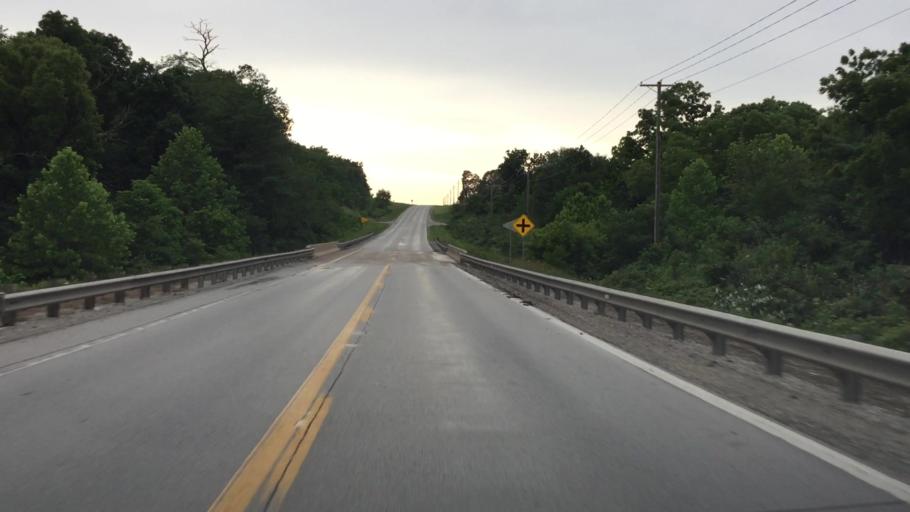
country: US
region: Illinois
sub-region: Hancock County
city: Hamilton
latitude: 40.3615
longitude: -91.3583
